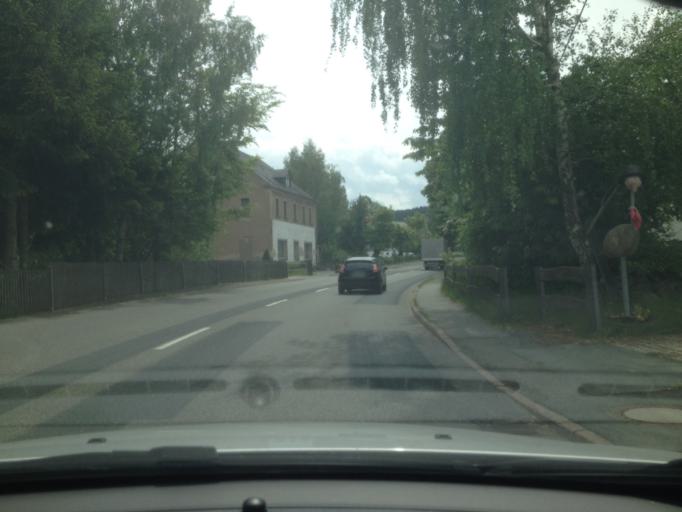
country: DE
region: Saxony
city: Stollberg
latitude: 50.6752
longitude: 12.7659
